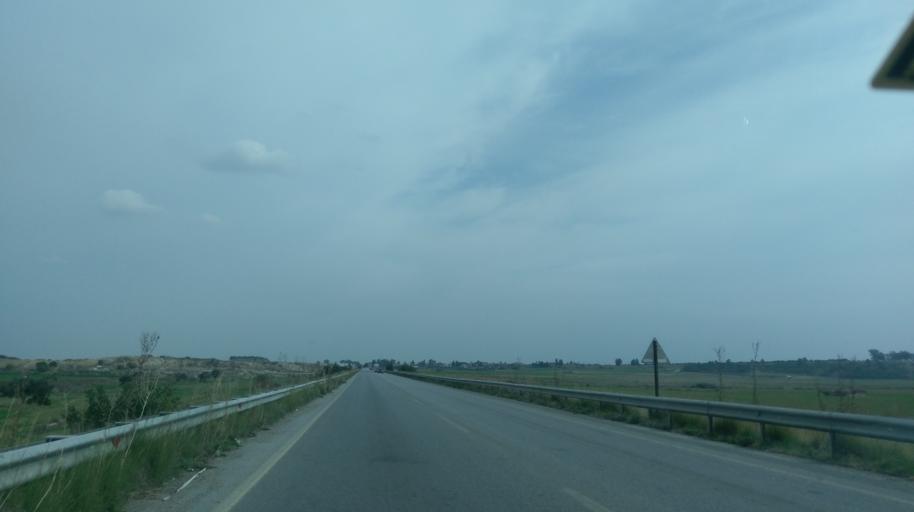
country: CY
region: Ammochostos
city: Lefkonoiko
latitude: 35.2610
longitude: 33.7629
